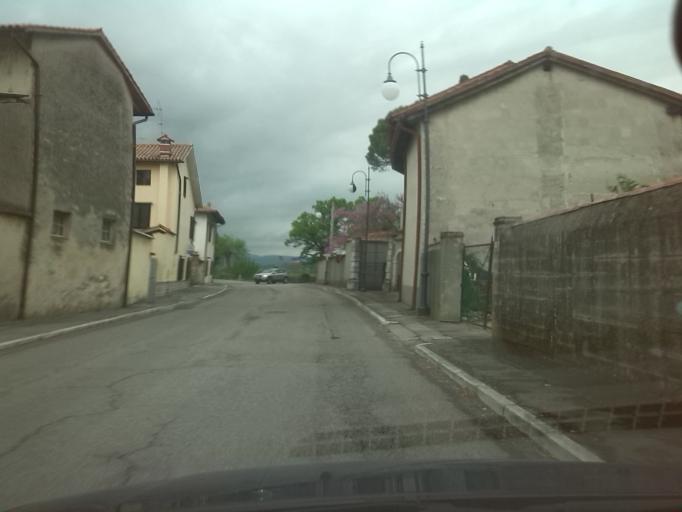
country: IT
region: Friuli Venezia Giulia
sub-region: Provincia di Gorizia
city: Farra d'Isonzo
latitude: 45.9132
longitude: 13.5190
